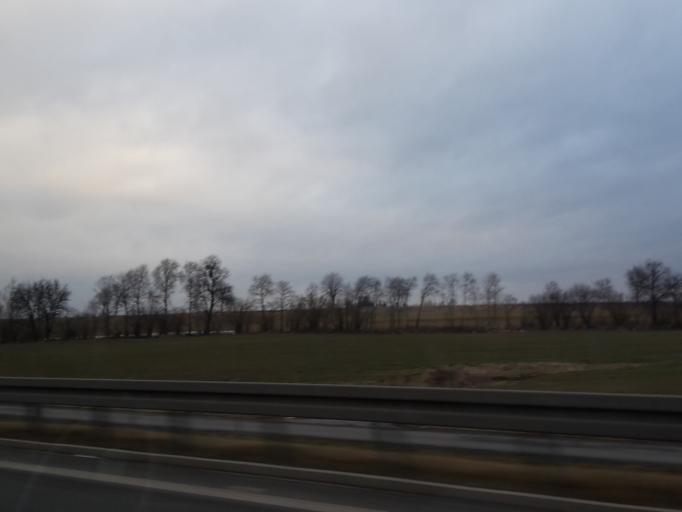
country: PL
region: Warmian-Masurian Voivodeship
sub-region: Powiat ostrodzki
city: Milomlyn
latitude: 53.8036
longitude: 19.7901
